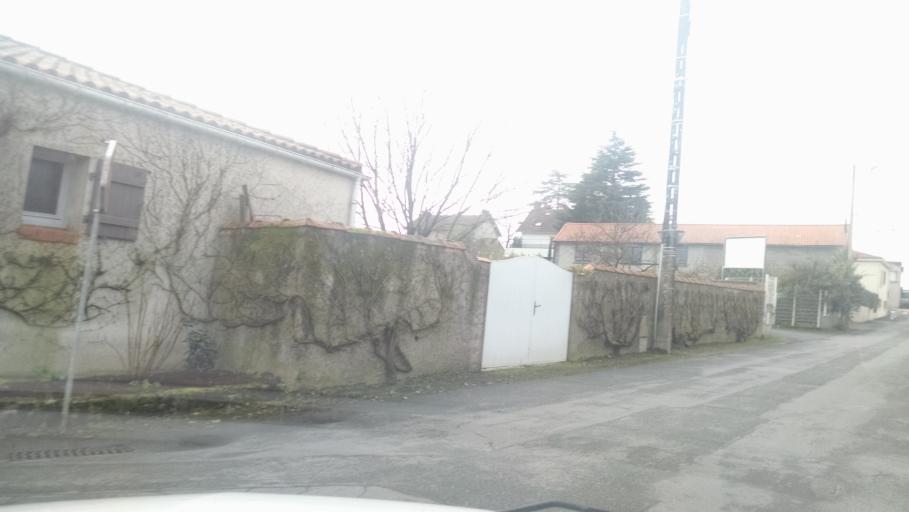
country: FR
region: Pays de la Loire
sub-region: Departement de la Loire-Atlantique
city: Clisson
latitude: 47.0831
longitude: -1.2788
